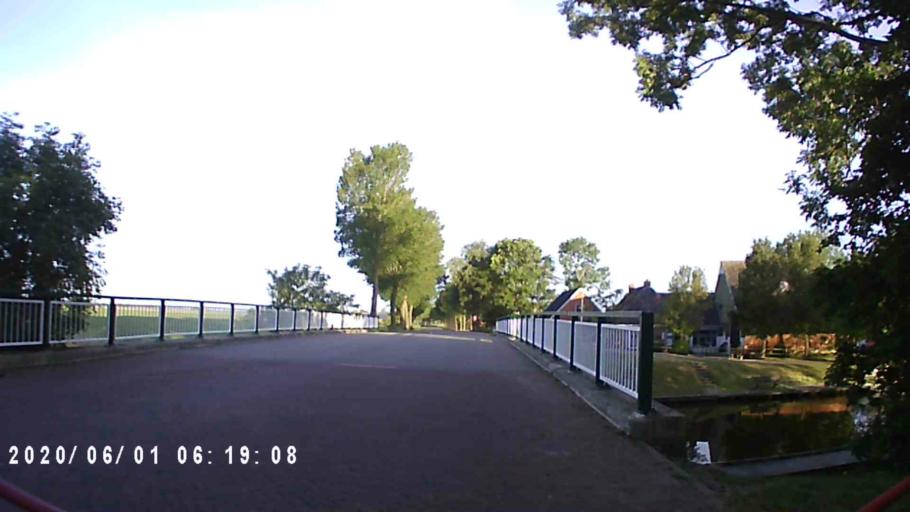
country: NL
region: Groningen
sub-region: Gemeente Grootegast
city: Grootegast
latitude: 53.2658
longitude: 6.2437
